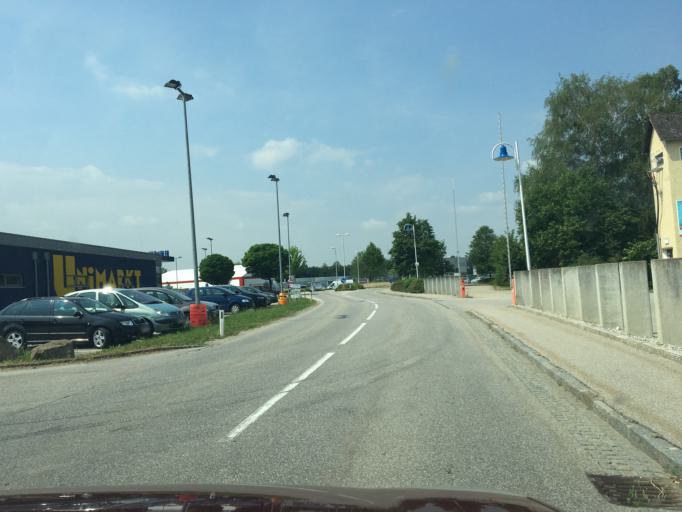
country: AT
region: Upper Austria
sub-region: Politischer Bezirk Scharding
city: Sankt Marienkirchen bei Schaerding
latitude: 48.3173
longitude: 13.4270
